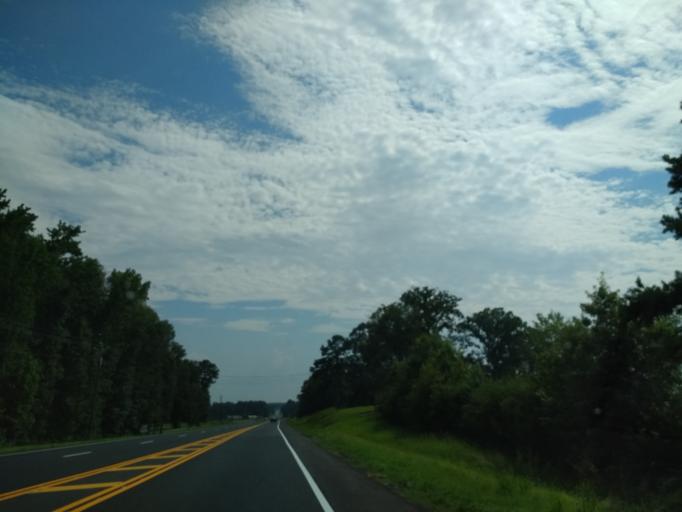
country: US
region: Georgia
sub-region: White County
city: Cleveland
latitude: 34.4873
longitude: -83.7602
